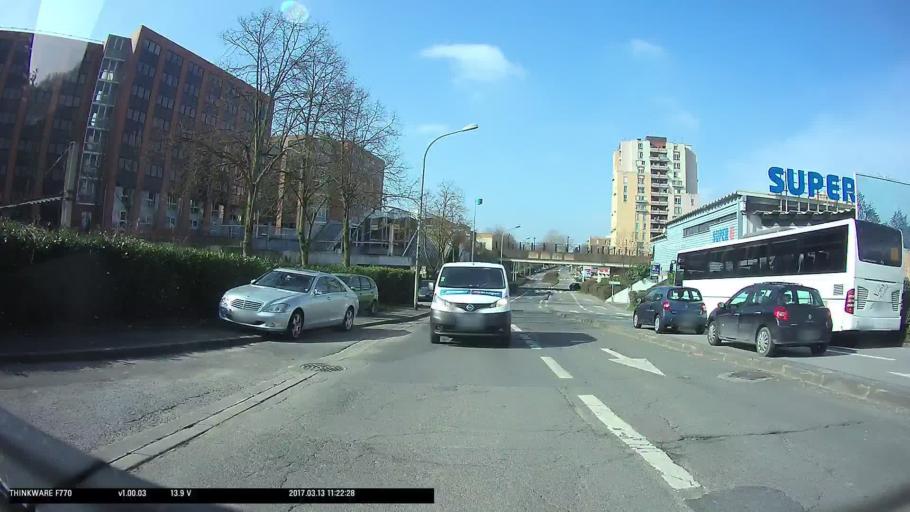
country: FR
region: Ile-de-France
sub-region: Departement de Seine-Saint-Denis
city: Noisy-le-Grand
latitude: 48.8430
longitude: 2.5792
